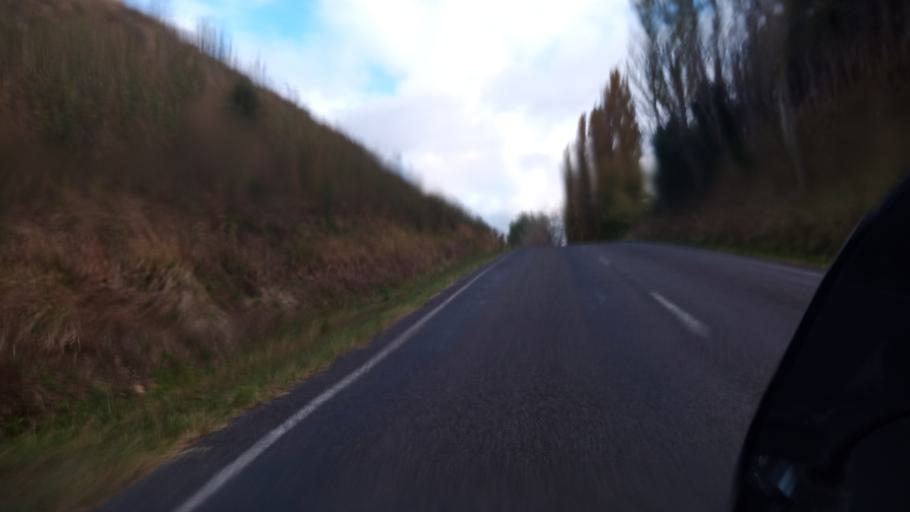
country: NZ
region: Gisborne
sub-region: Gisborne District
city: Gisborne
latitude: -38.5884
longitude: 177.7632
